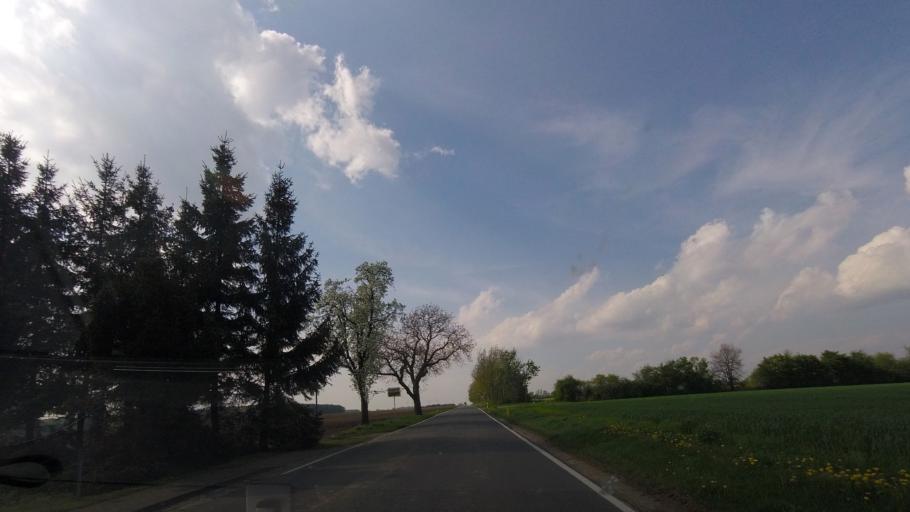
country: DE
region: Saxony-Anhalt
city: Seyda
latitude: 51.9595
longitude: 12.8800
